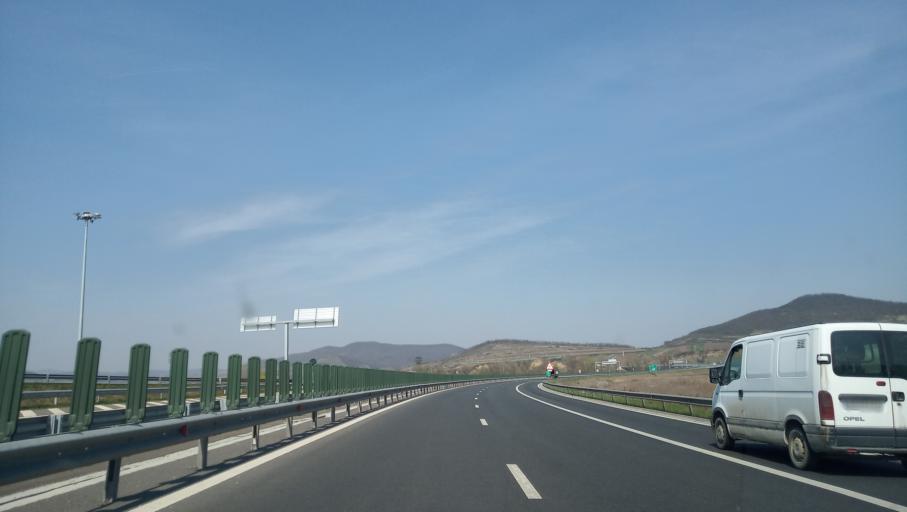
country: RO
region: Alba
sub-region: Municipiul Aiud
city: Aiud
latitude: 46.3302
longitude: 23.7292
